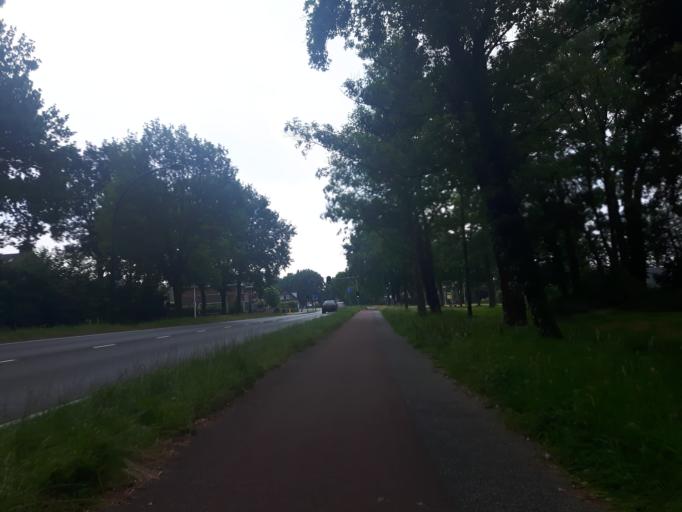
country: NL
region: Overijssel
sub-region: Gemeente Hengelo
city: Hengelo
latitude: 52.2773
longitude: 6.7814
